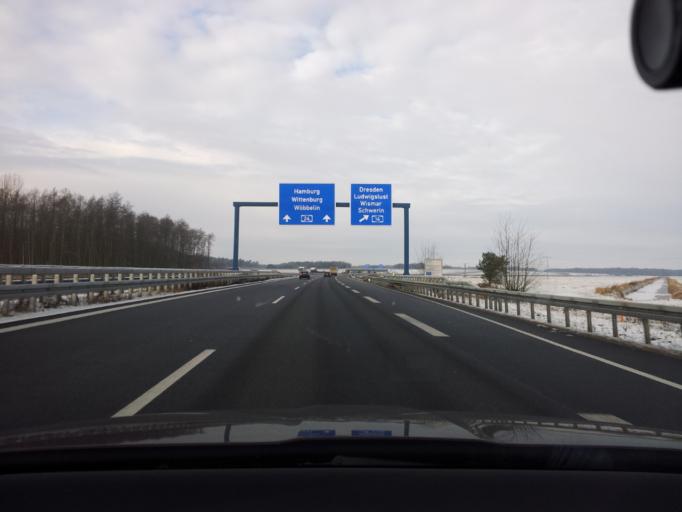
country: DE
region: Mecklenburg-Vorpommern
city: Neustadt-Glewe
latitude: 53.4199
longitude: 11.5324
